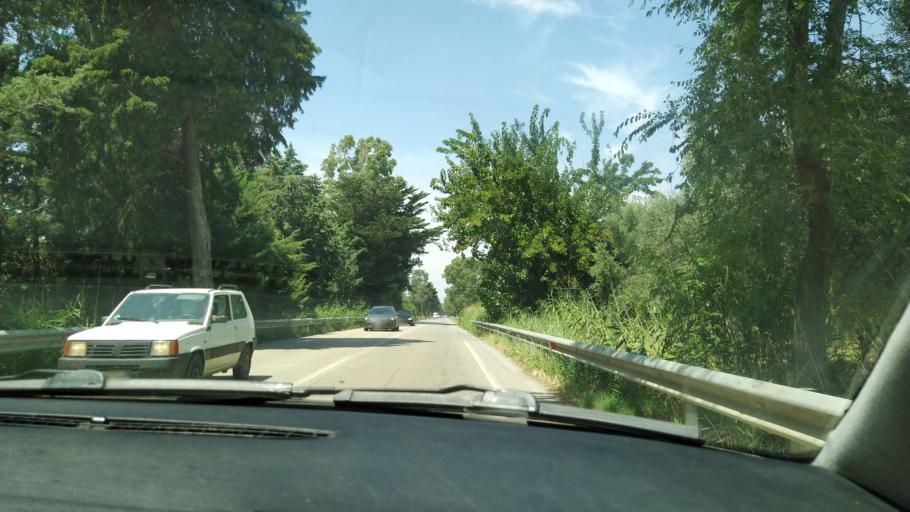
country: IT
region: Apulia
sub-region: Provincia di Taranto
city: Marina di Ginosa
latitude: 40.3733
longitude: 16.8027
